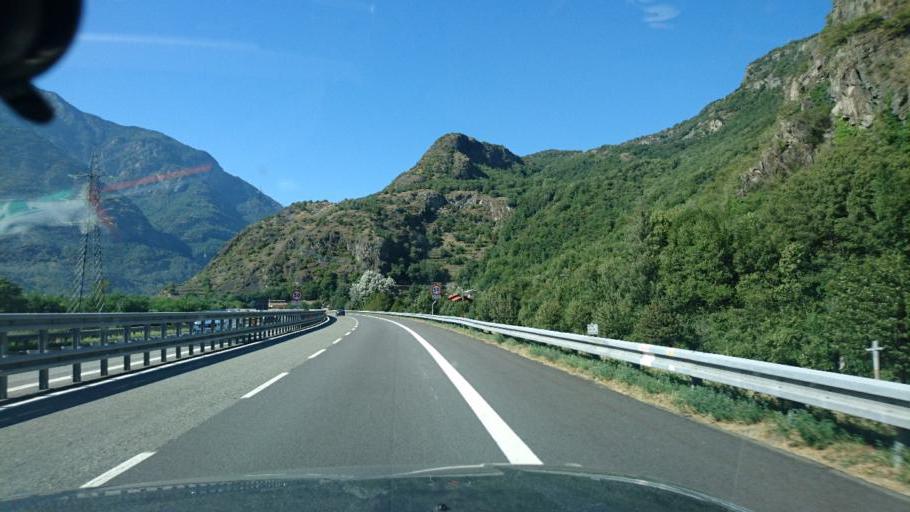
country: IT
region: Aosta Valley
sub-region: Valle d'Aosta
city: Verres
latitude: 45.6730
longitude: 7.6822
